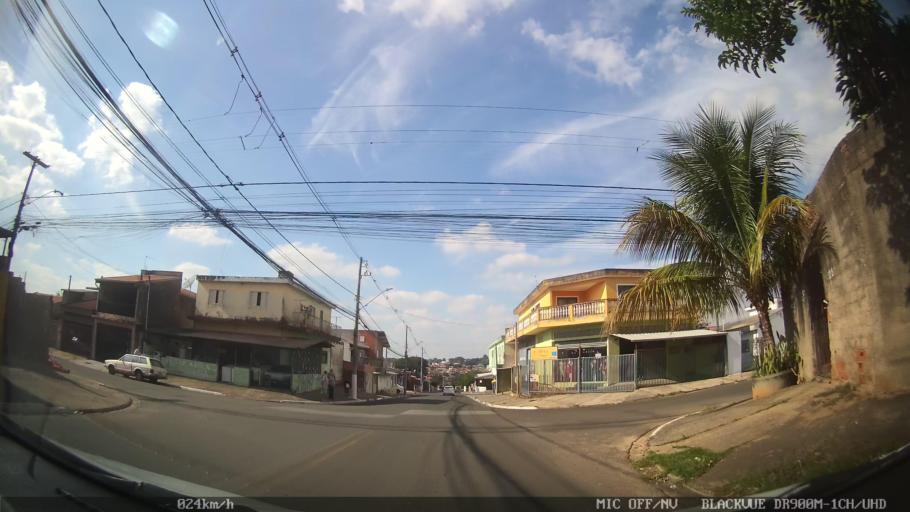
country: BR
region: Sao Paulo
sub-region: Hortolandia
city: Hortolandia
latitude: -22.9041
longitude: -47.2380
